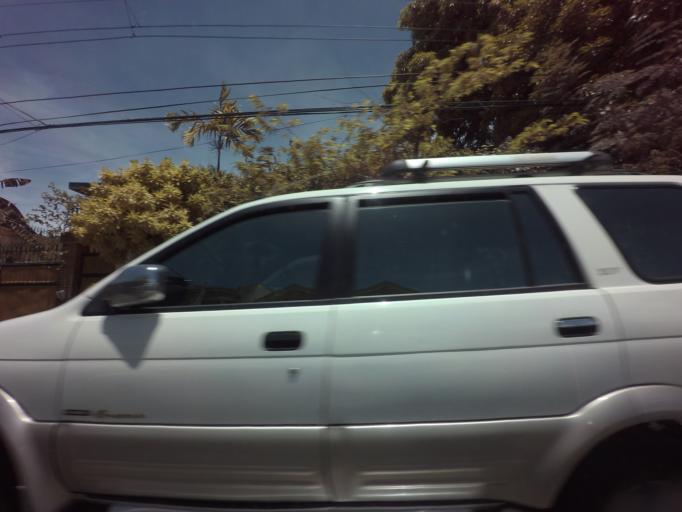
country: PH
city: Sambayanihan People's Village
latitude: 14.4873
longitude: 121.0362
